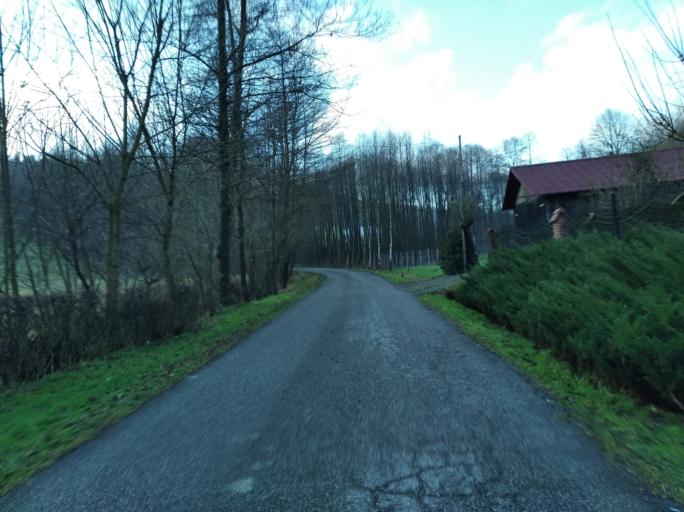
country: PL
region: Subcarpathian Voivodeship
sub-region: Powiat strzyzowski
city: Czudec
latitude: 49.9497
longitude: 21.7980
